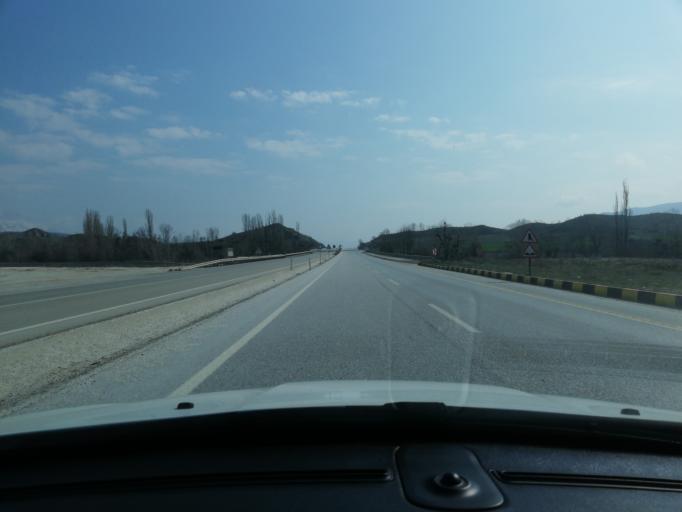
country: TR
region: Cankiri
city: Beloren
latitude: 40.8766
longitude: 33.5081
